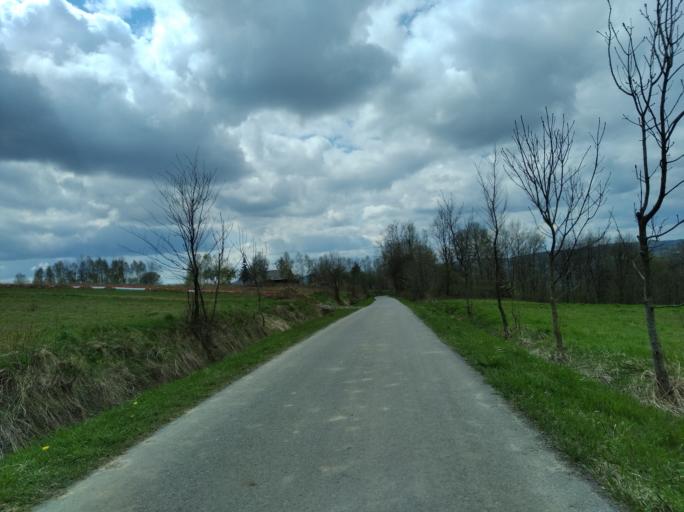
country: PL
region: Subcarpathian Voivodeship
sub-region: Powiat rzeszowski
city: Lubenia
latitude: 49.8901
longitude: 21.9306
